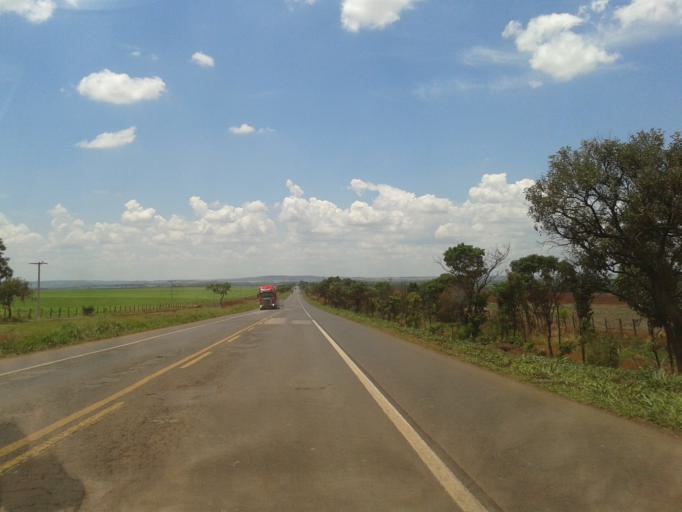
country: BR
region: Goias
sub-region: Goiatuba
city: Goiatuba
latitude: -18.2775
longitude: -49.6294
